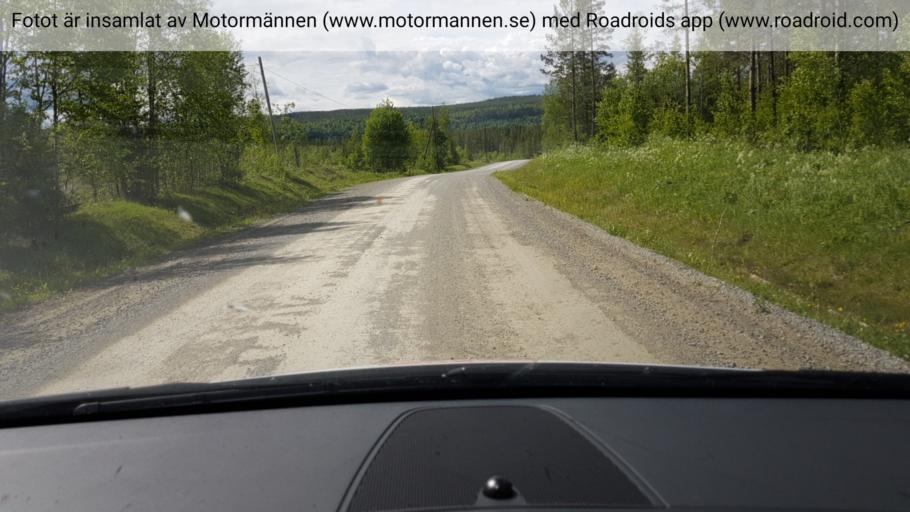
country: SE
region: Jaemtland
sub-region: Bergs Kommun
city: Hoverberg
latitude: 62.9644
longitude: 14.2600
